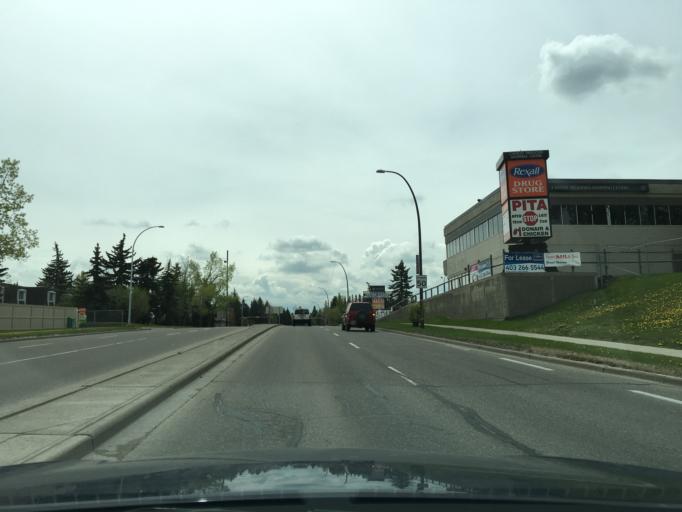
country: CA
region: Alberta
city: Calgary
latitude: 50.9498
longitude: -114.0846
